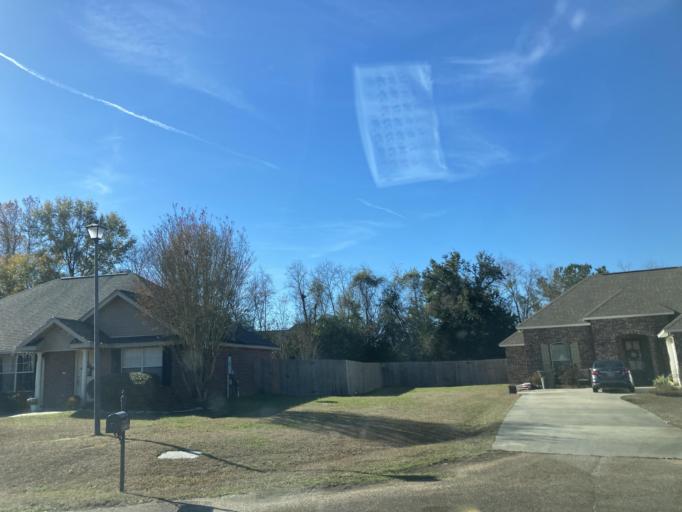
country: US
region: Mississippi
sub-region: Forrest County
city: Petal
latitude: 31.3182
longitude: -89.1876
